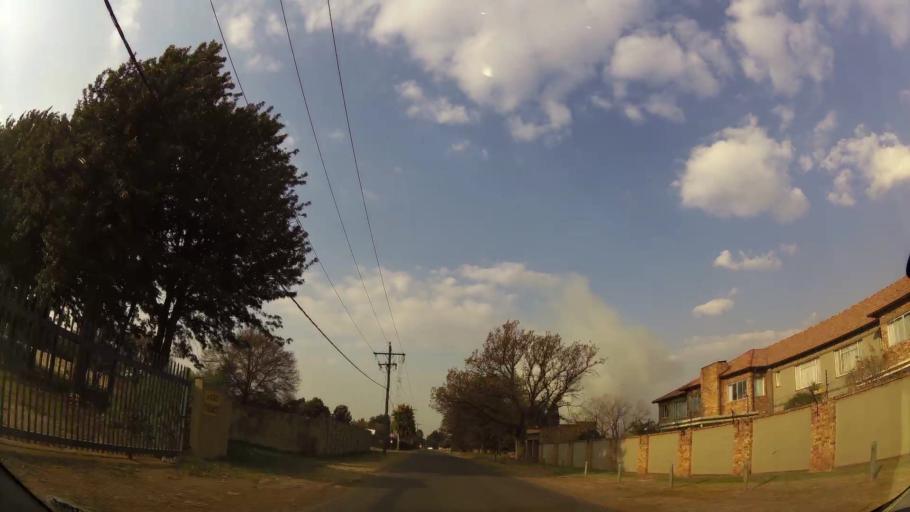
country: ZA
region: Gauteng
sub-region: Ekurhuleni Metropolitan Municipality
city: Benoni
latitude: -26.1224
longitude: 28.2908
